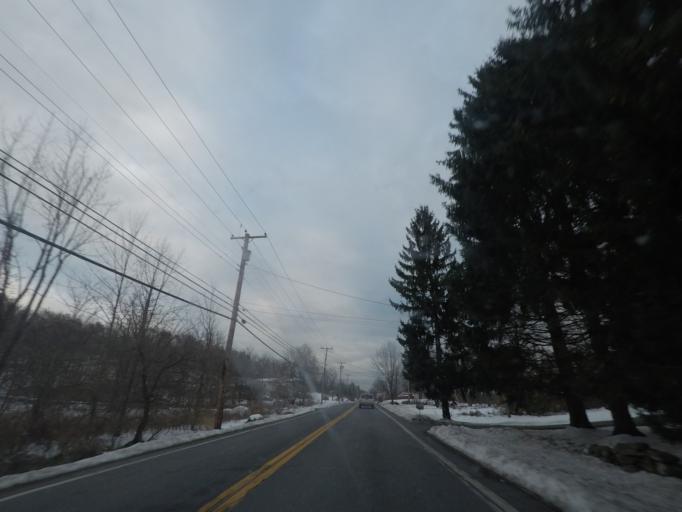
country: US
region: New York
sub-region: Ulster County
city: Plattekill
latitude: 41.5980
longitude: -74.0722
